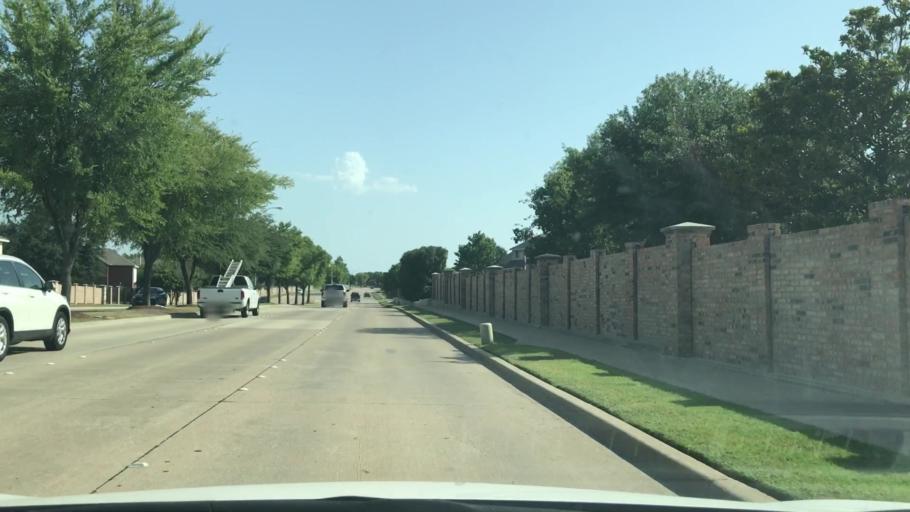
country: US
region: Texas
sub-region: Collin County
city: Allen
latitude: 33.0929
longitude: -96.7488
